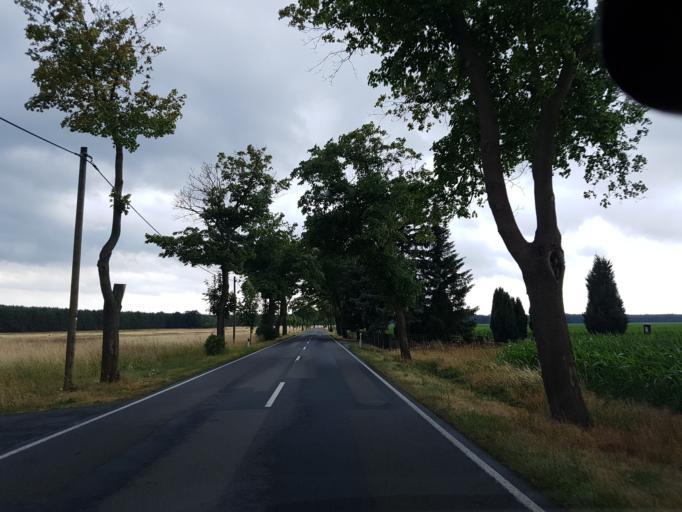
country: DE
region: Saxony-Anhalt
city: Seyda
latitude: 51.9031
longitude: 12.9392
